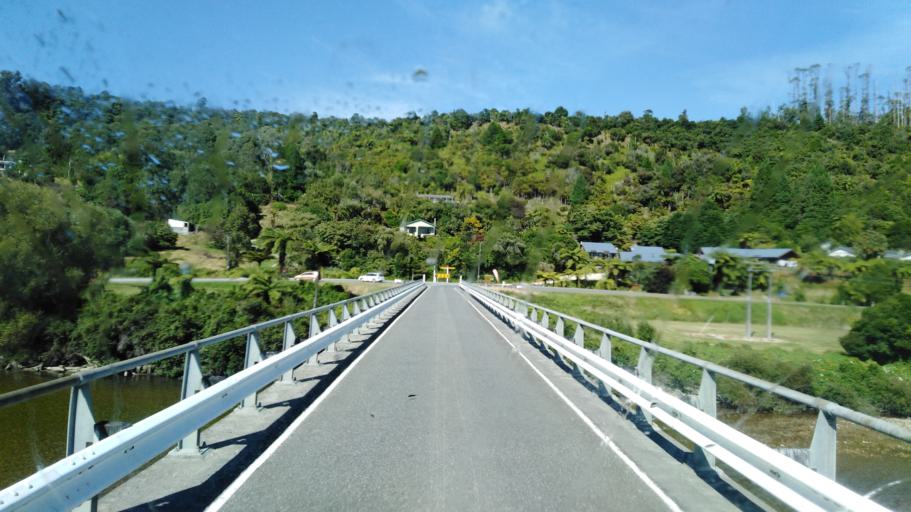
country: NZ
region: West Coast
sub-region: Buller District
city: Westport
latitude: -41.2610
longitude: 172.1312
